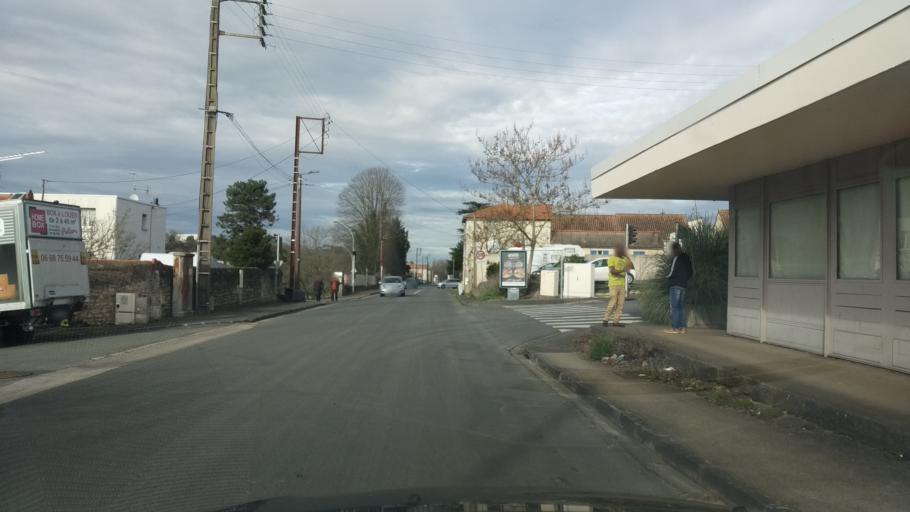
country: FR
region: Poitou-Charentes
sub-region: Departement de la Vienne
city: Poitiers
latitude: 46.5969
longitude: 0.3421
